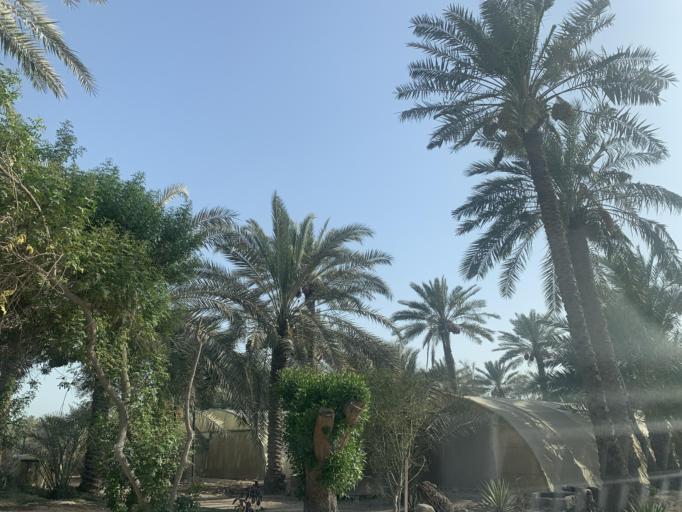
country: BH
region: Manama
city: Jidd Hafs
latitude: 26.1968
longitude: 50.4597
